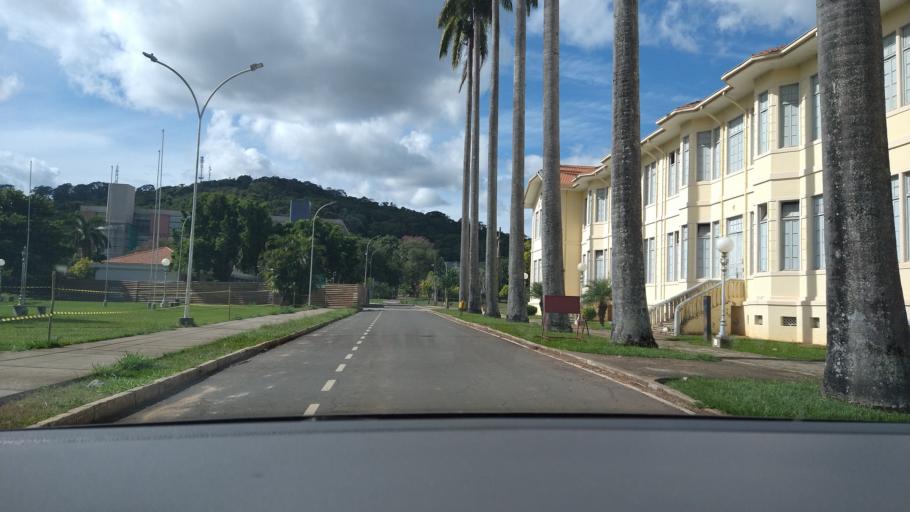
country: BR
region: Minas Gerais
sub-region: Vicosa
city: Vicosa
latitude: -20.7627
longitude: -42.8688
